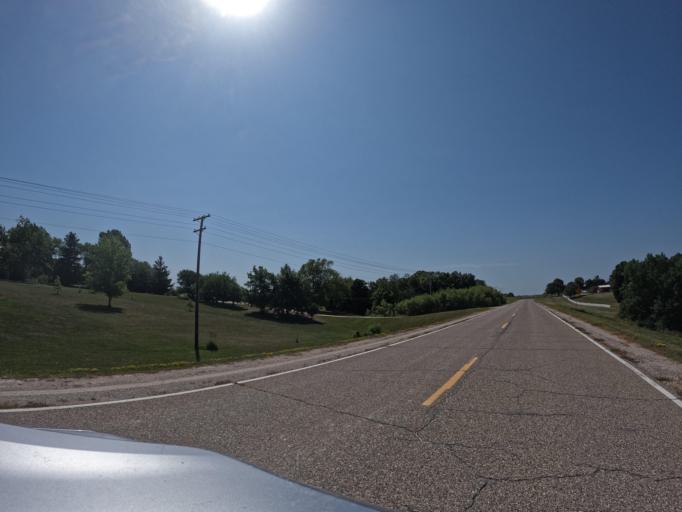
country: US
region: Iowa
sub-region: Henry County
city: Mount Pleasant
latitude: 40.9330
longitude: -91.5403
